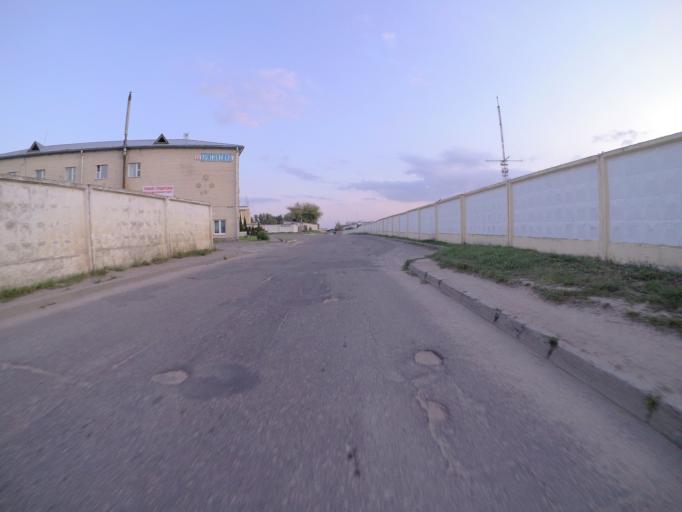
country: BY
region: Grodnenskaya
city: Hrodna
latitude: 53.7054
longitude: 23.8281
